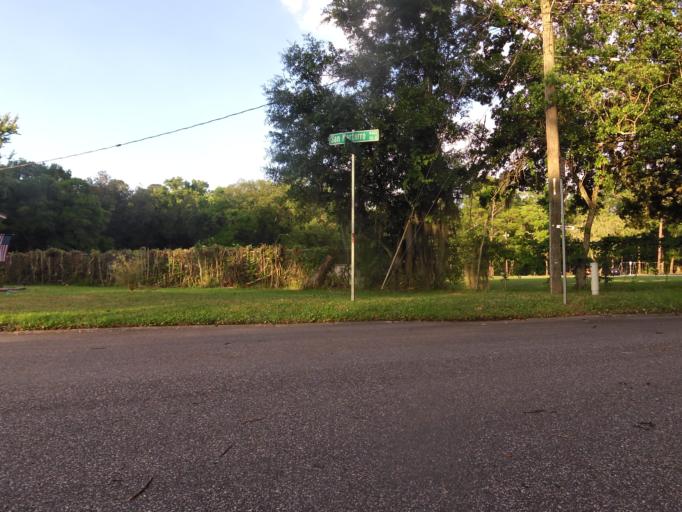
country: US
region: Florida
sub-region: Duval County
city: Jacksonville
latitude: 30.2280
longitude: -81.6074
